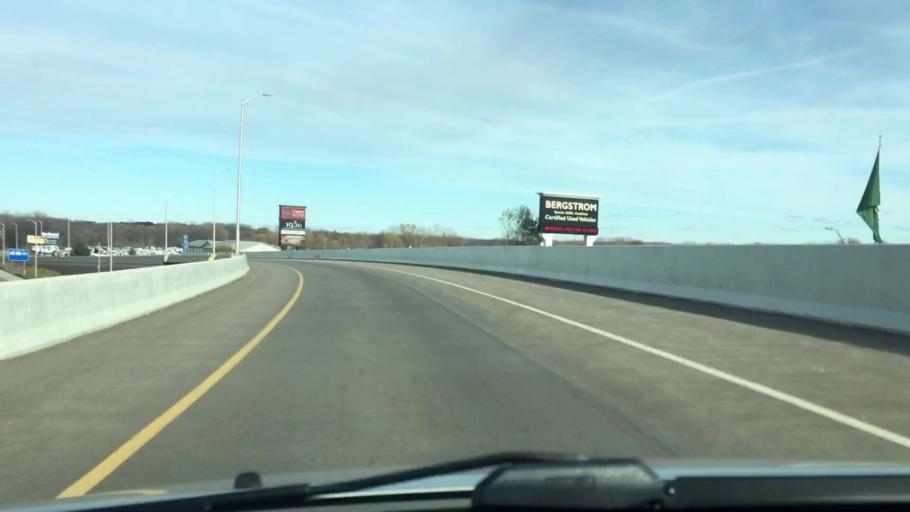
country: US
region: Wisconsin
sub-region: Brown County
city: Howard
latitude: 44.5401
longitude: -88.0755
